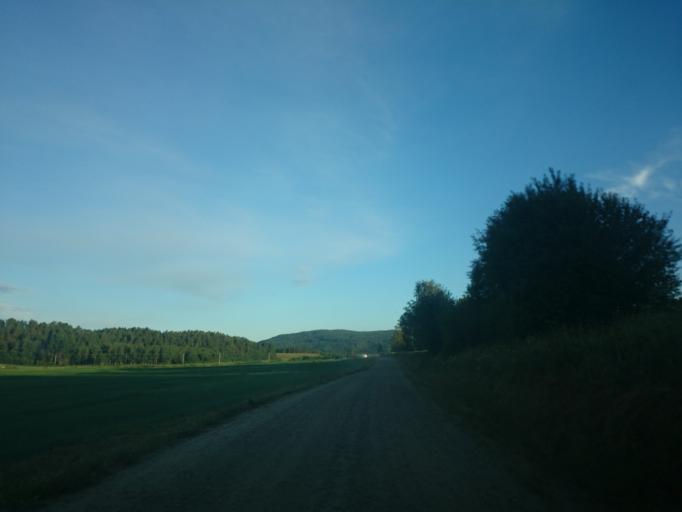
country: SE
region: Vaesternorrland
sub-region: Kramfors Kommun
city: Bollstabruk
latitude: 63.0683
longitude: 17.7345
